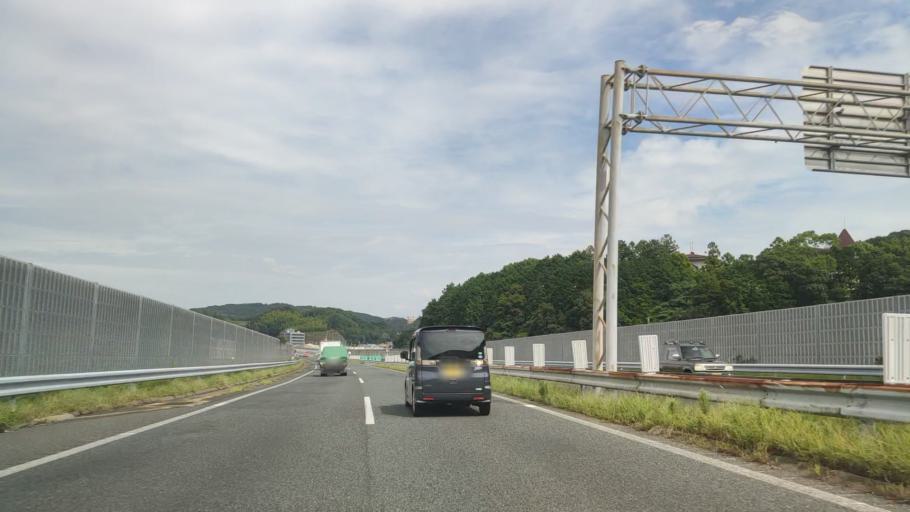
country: JP
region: Wakayama
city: Kainan
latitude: 34.1486
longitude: 135.2260
